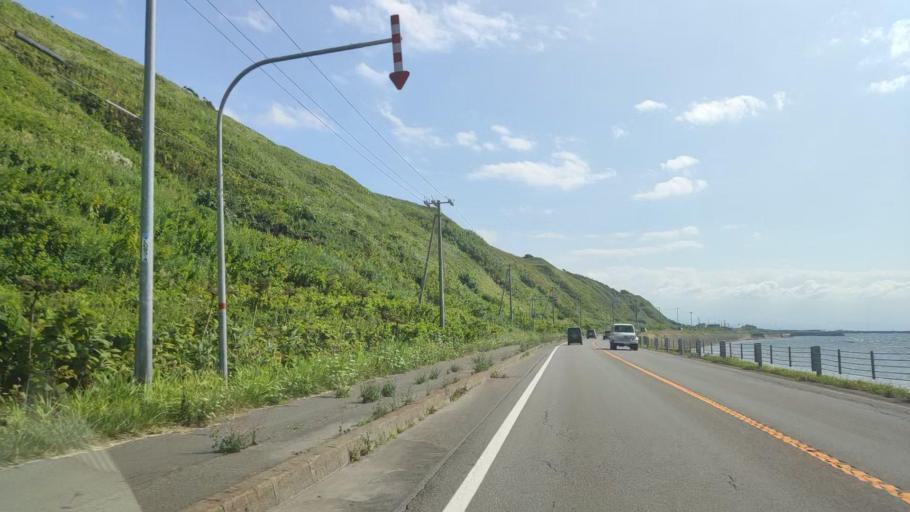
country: JP
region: Hokkaido
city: Rumoi
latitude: 43.9907
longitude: 141.6510
